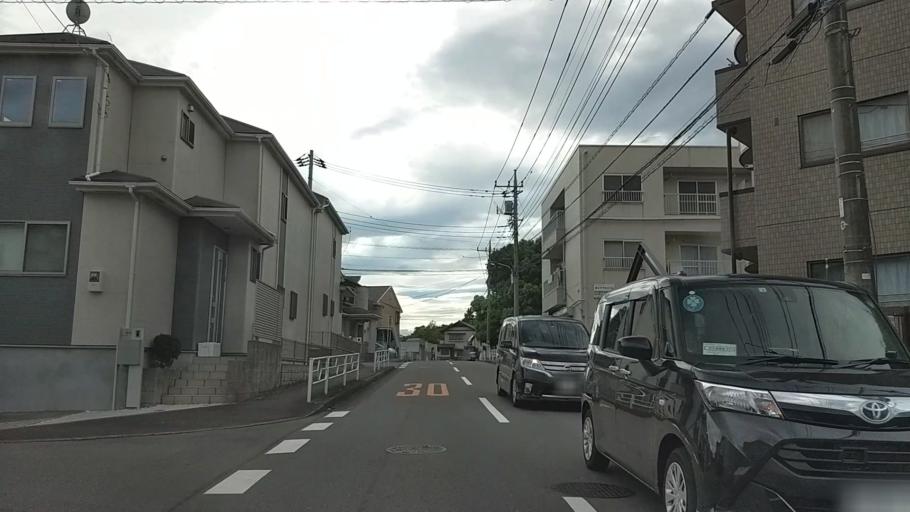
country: JP
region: Tokyo
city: Hachioji
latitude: 35.6363
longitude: 139.3103
